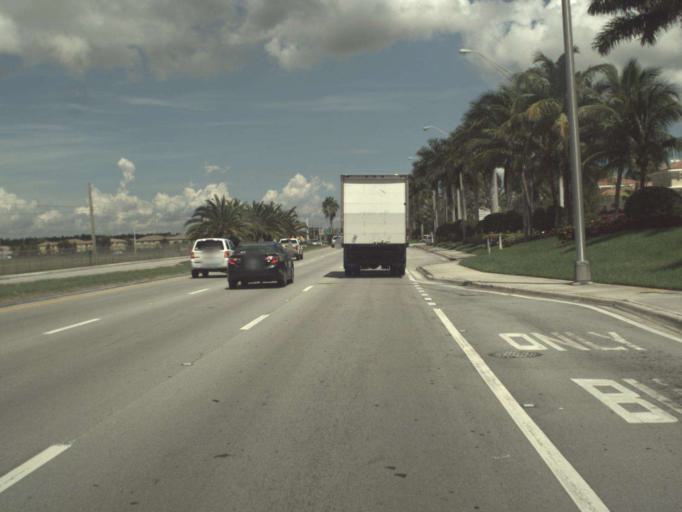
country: US
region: Florida
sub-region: Miami-Dade County
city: Three Lakes
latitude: 25.6527
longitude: -80.4156
